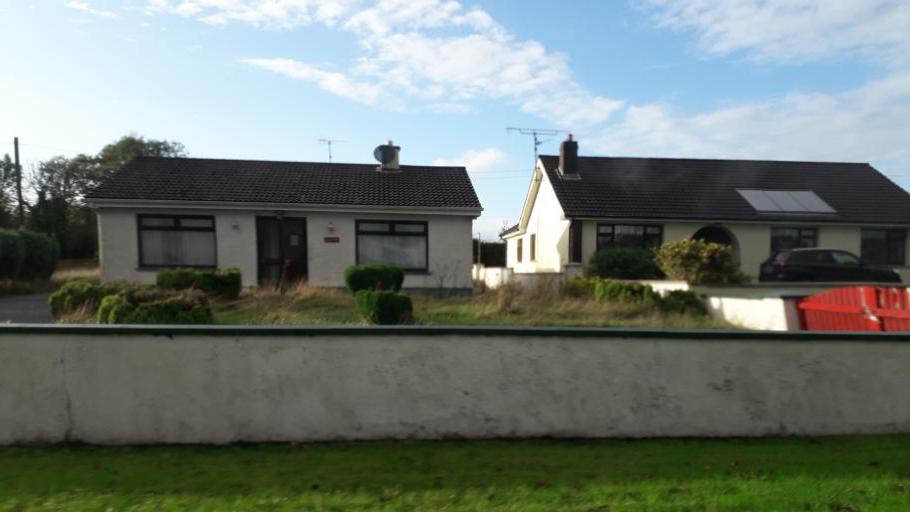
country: IE
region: Connaught
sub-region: Roscommon
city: Roscommon
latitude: 53.7748
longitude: -8.1148
